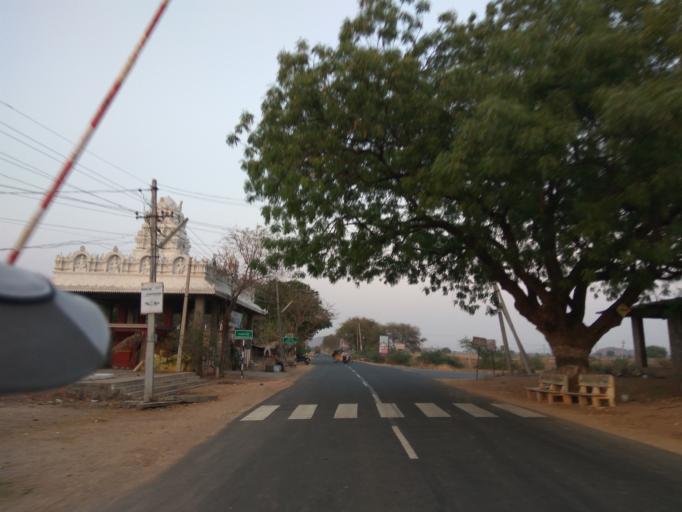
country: IN
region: Andhra Pradesh
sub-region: Prakasam
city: Markapur
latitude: 15.7533
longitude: 79.2259
